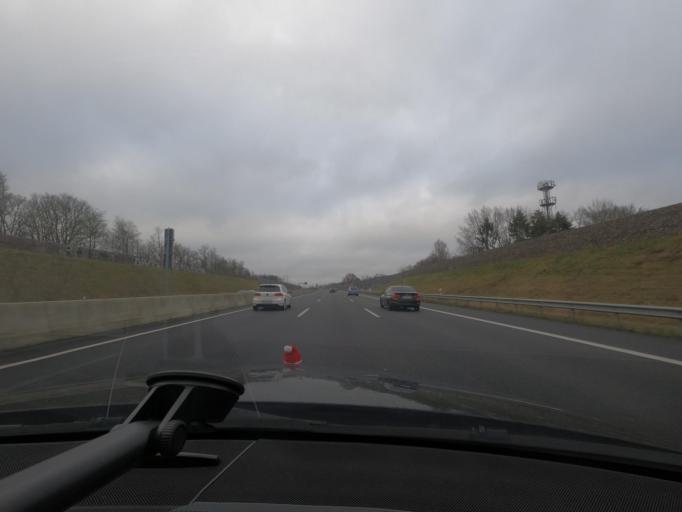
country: DE
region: Schleswig-Holstein
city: Ellerau
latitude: 53.7505
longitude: 9.9497
